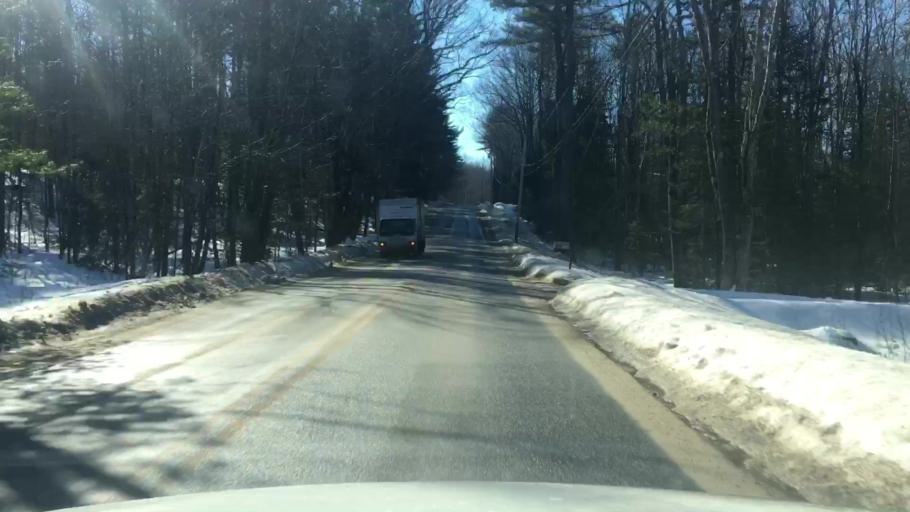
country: US
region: Maine
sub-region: Cumberland County
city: North Windham
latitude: 43.8592
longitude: -70.3436
